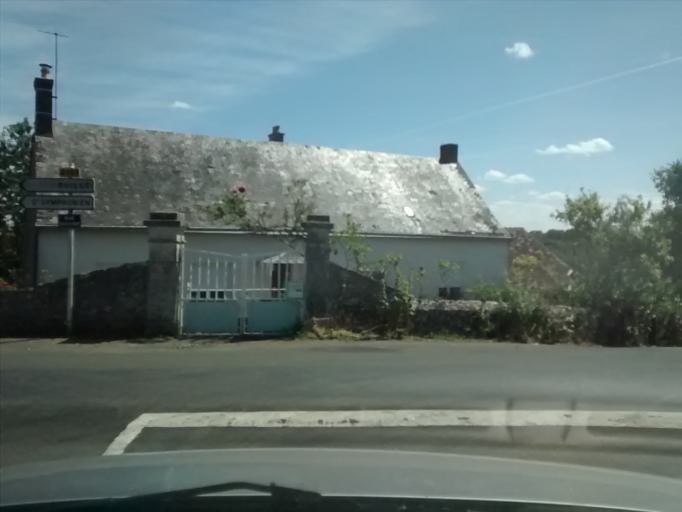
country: FR
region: Pays de la Loire
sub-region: Departement de la Sarthe
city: Loue
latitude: 48.0366
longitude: -0.1151
